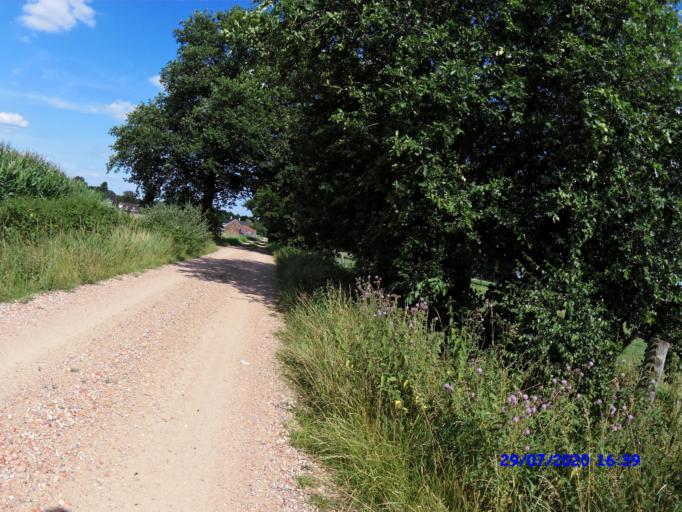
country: BE
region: Flanders
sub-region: Provincie Antwerpen
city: Oostmalle
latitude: 51.3078
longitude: 4.7742
